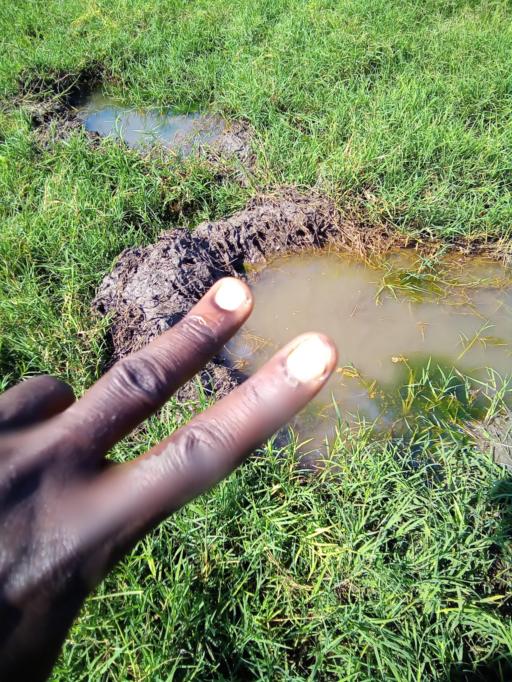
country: KE
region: Homa Bay
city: Homa Bay
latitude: -0.4621
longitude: 34.1862
